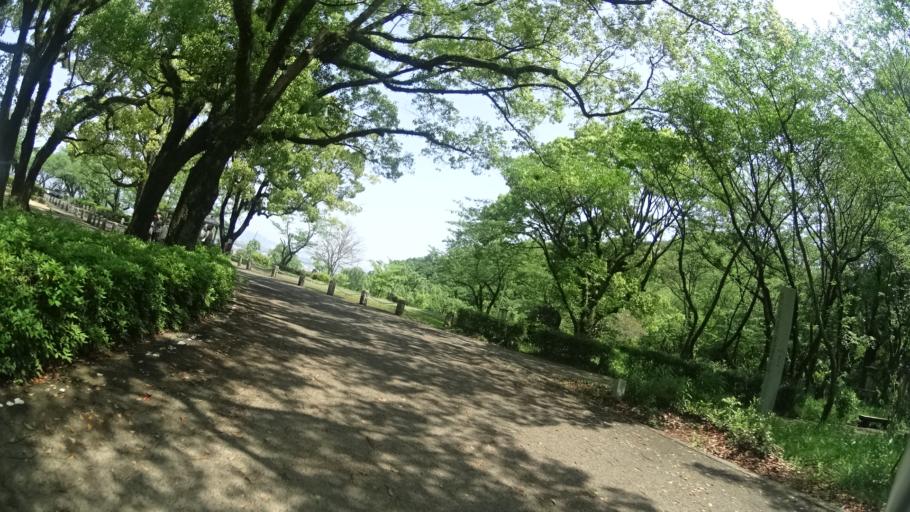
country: JP
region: Tokushima
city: Tokushima-shi
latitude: 34.0686
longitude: 134.5143
